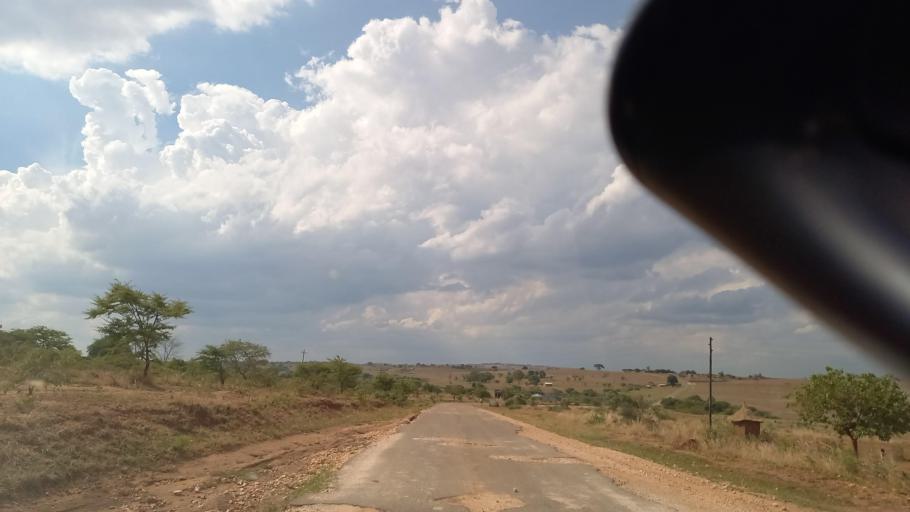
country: ZM
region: Lusaka
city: Kafue
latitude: -16.2140
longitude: 28.1129
